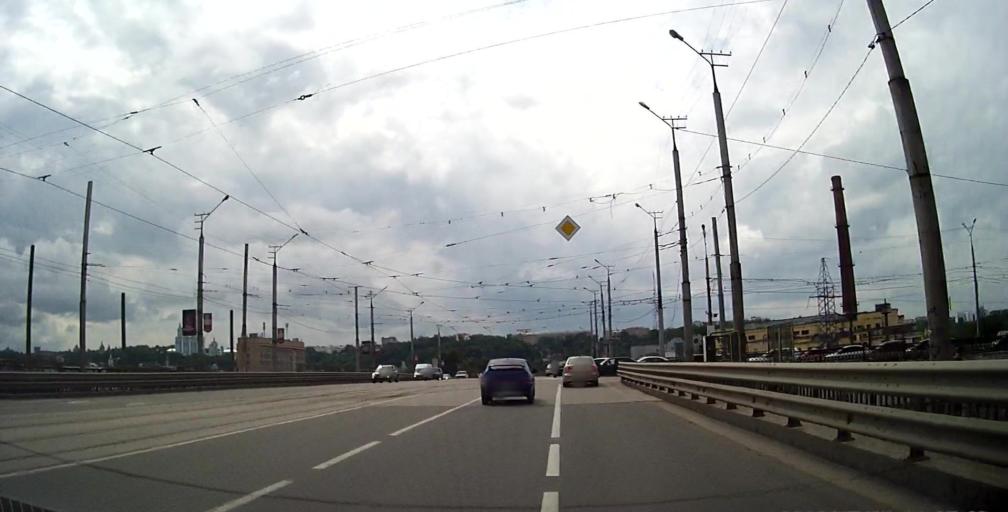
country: RU
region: Smolensk
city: Smolensk
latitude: 54.7979
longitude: 32.0445
